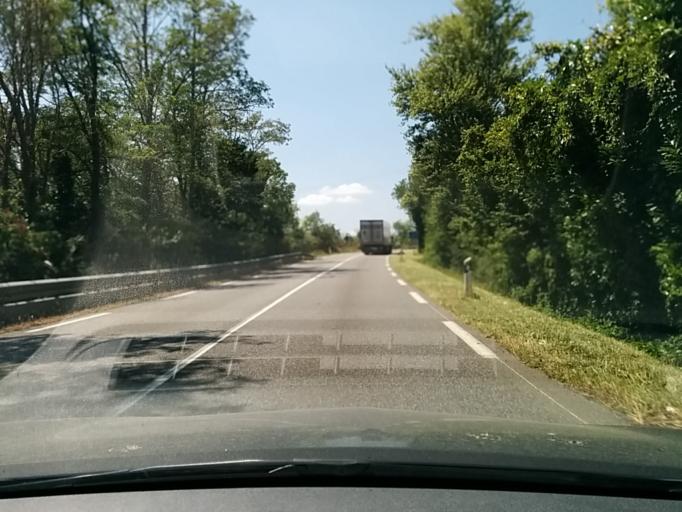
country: FR
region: Midi-Pyrenees
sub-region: Departement du Gers
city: Gimont
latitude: 43.6305
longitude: 0.8620
